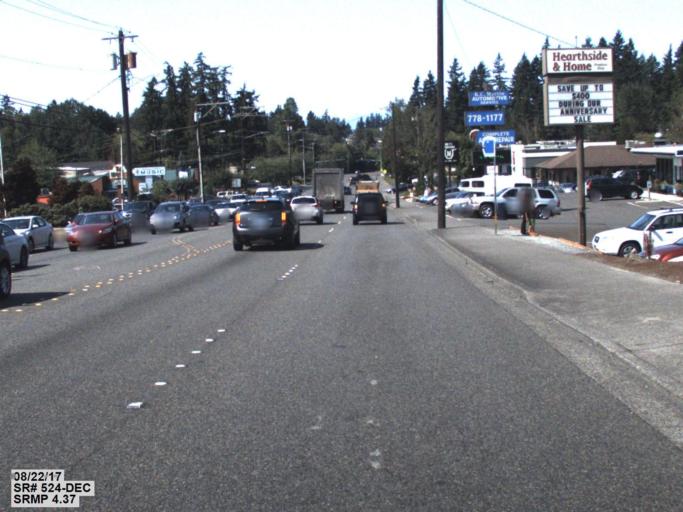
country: US
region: Washington
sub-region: Snohomish County
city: Alderwood Manor
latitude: 47.8211
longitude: -122.2980
